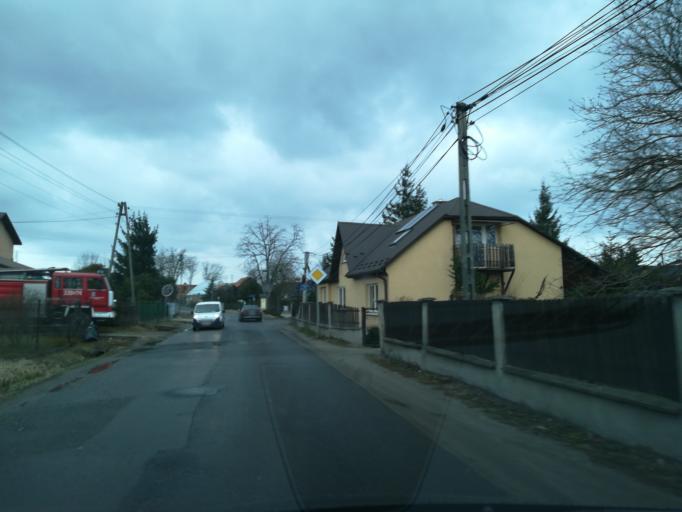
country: PL
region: Lesser Poland Voivodeship
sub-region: Krakow
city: Sidzina
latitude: 49.9901
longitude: 19.8656
